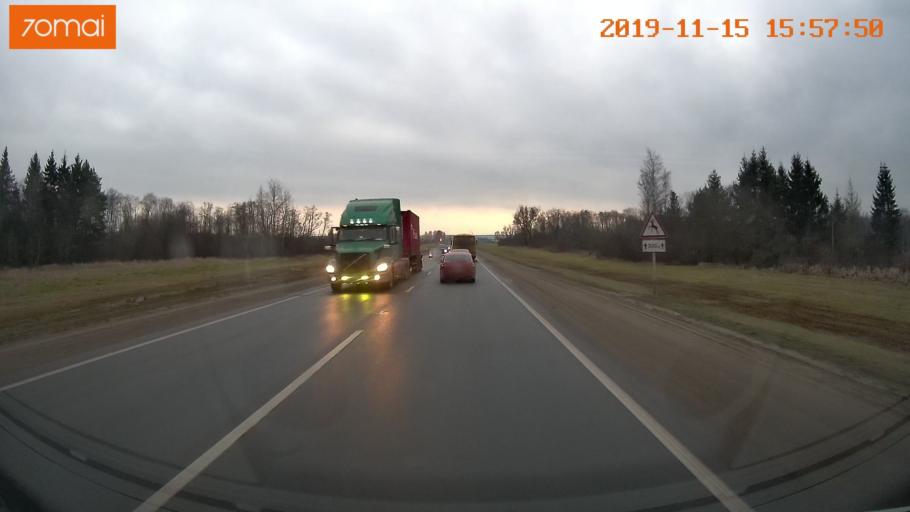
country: RU
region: Jaroslavl
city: Yaroslavl
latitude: 57.8263
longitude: 39.9600
